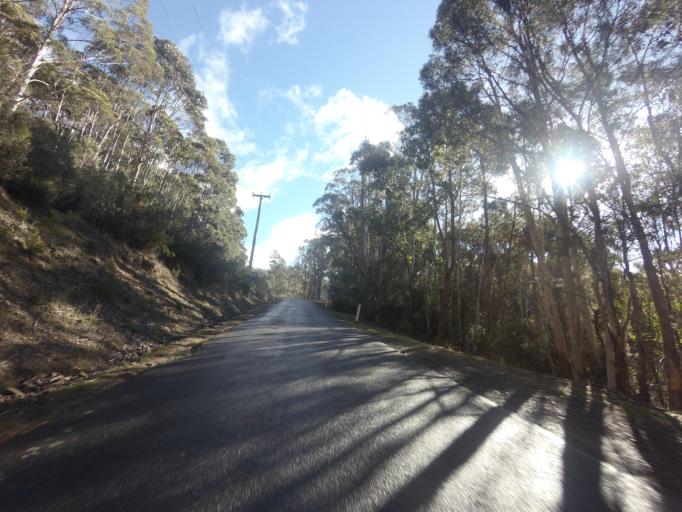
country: AU
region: Tasmania
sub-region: Glenorchy
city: Berriedale
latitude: -42.8374
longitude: 147.1739
